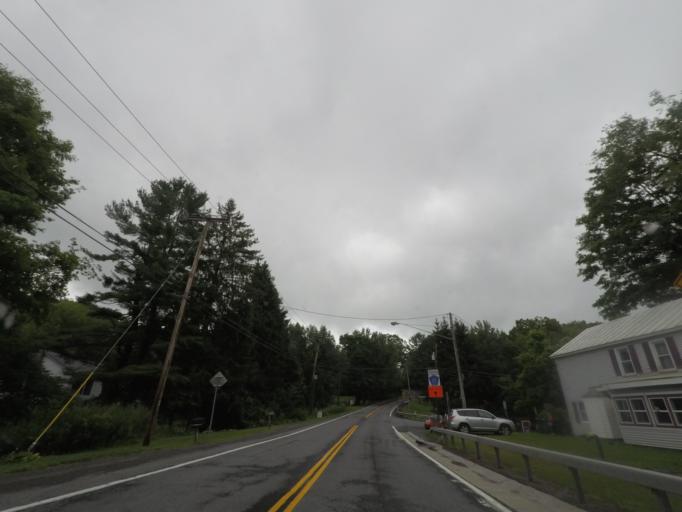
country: US
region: New York
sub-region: Rensselaer County
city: Averill Park
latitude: 42.5855
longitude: -73.4853
